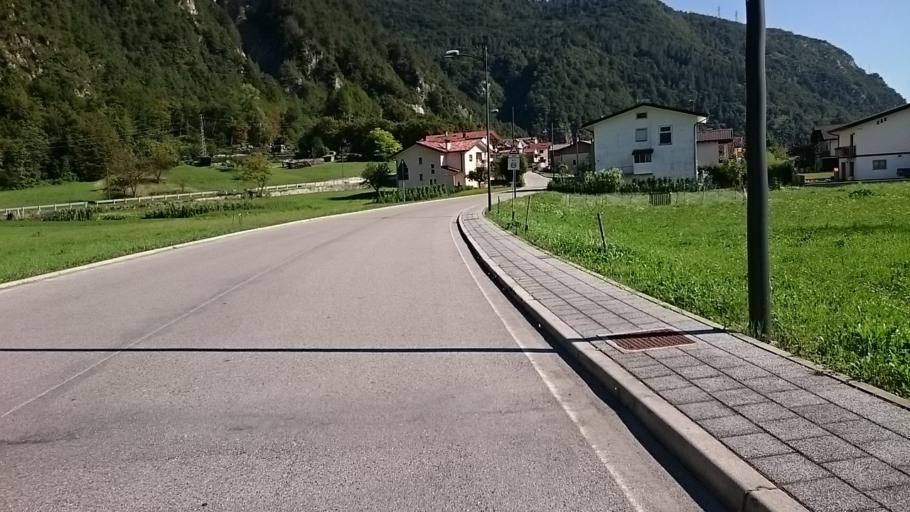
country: IT
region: Veneto
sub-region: Provincia di Belluno
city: Soverzene
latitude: 46.2076
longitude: 12.3026
